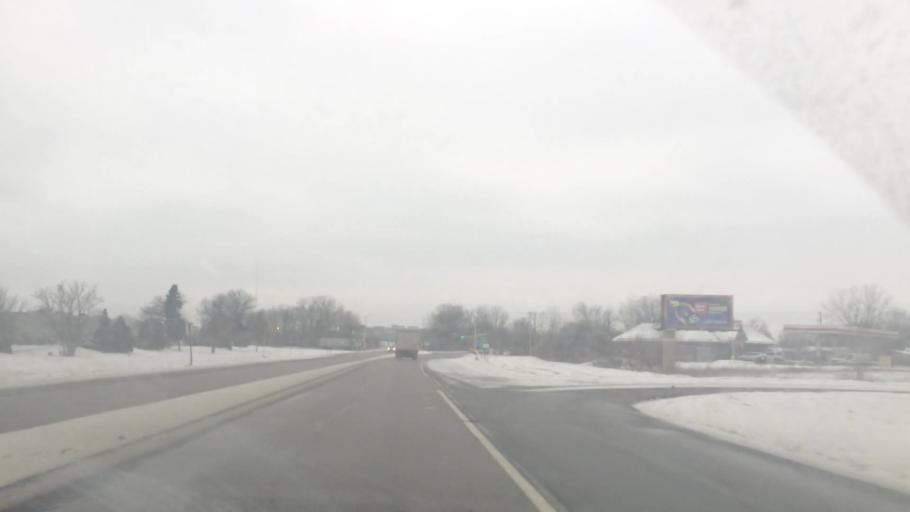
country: US
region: Minnesota
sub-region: Anoka County
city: Lexington
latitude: 45.1305
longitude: -93.1814
